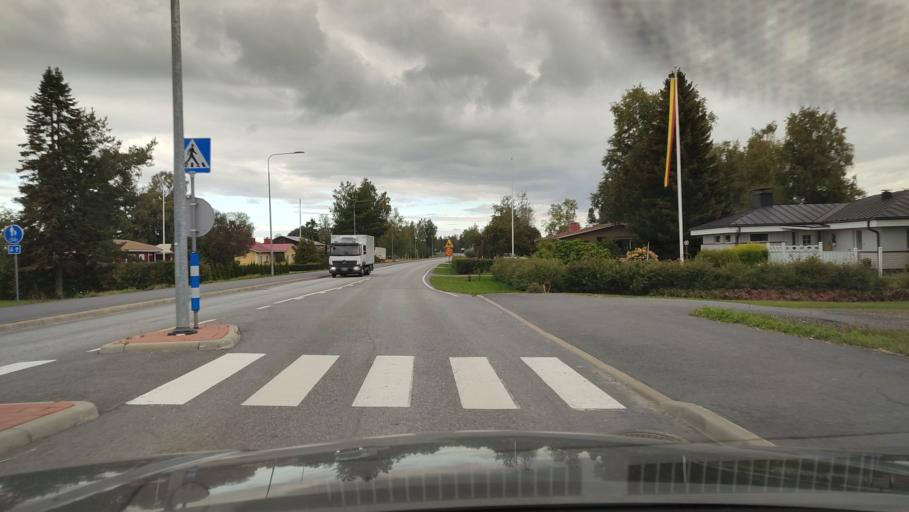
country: FI
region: Ostrobothnia
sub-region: Sydosterbotten
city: Kristinestad
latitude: 62.2521
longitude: 21.5224
